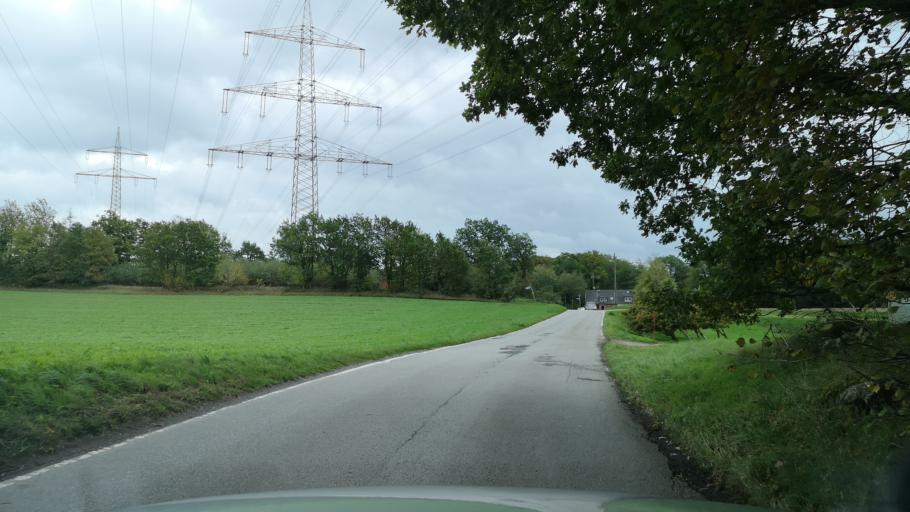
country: DE
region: North Rhine-Westphalia
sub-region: Regierungsbezirk Dusseldorf
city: Velbert
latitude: 51.3708
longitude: 7.0520
